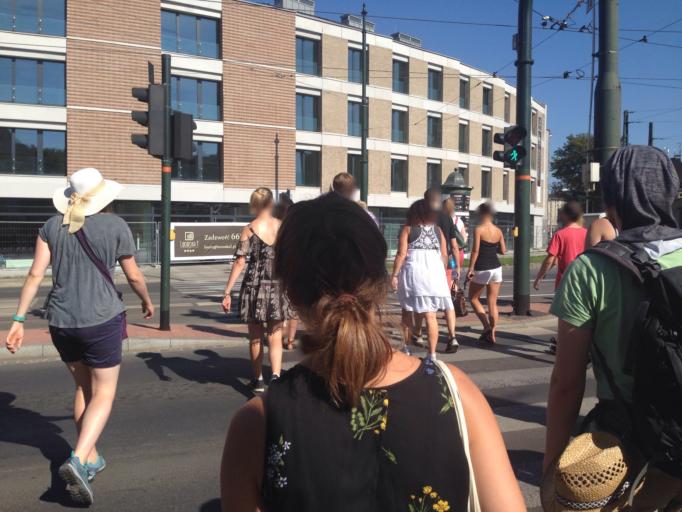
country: PL
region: Lesser Poland Voivodeship
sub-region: Krakow
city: Krakow
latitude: 50.0454
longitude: 19.9554
